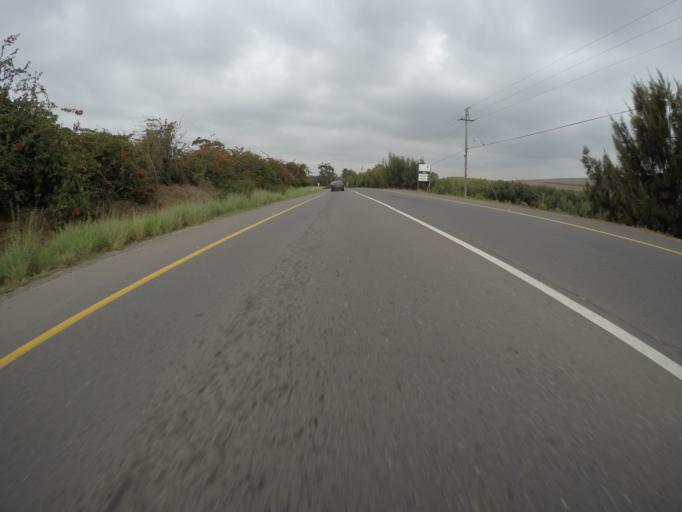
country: ZA
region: Western Cape
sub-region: City of Cape Town
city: Kraaifontein
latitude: -33.8400
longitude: 18.6071
